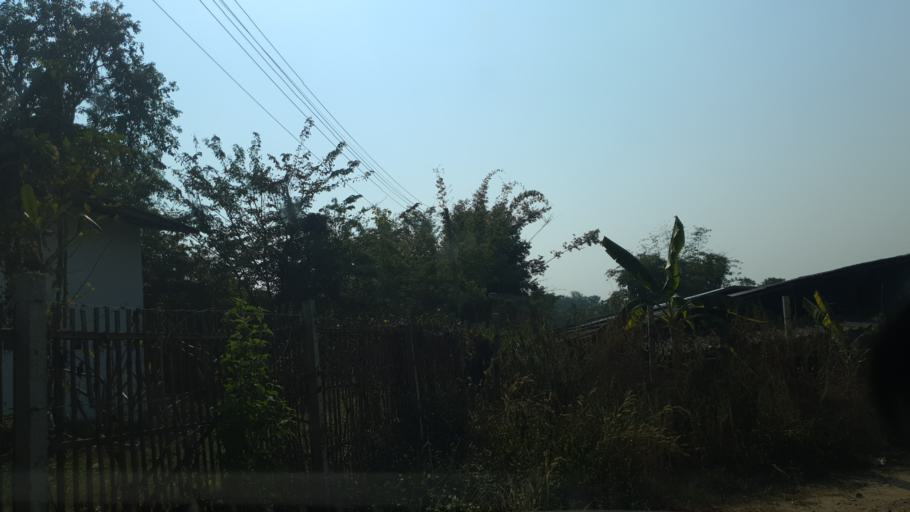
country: TH
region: Chiang Mai
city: Mae On
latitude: 18.7470
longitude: 99.2491
